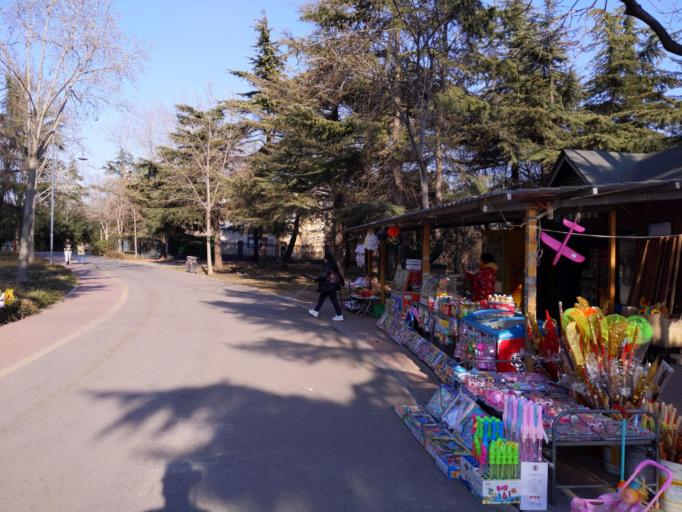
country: CN
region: Henan Sheng
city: Puyang
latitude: 35.7751
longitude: 114.9620
